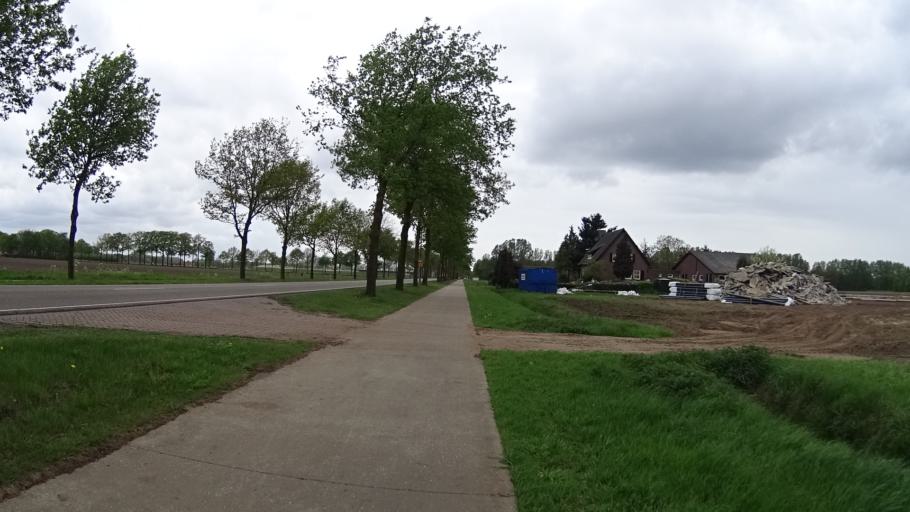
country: NL
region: North Brabant
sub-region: Gemeente Veghel
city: Keldonk
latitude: 51.6043
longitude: 5.5866
